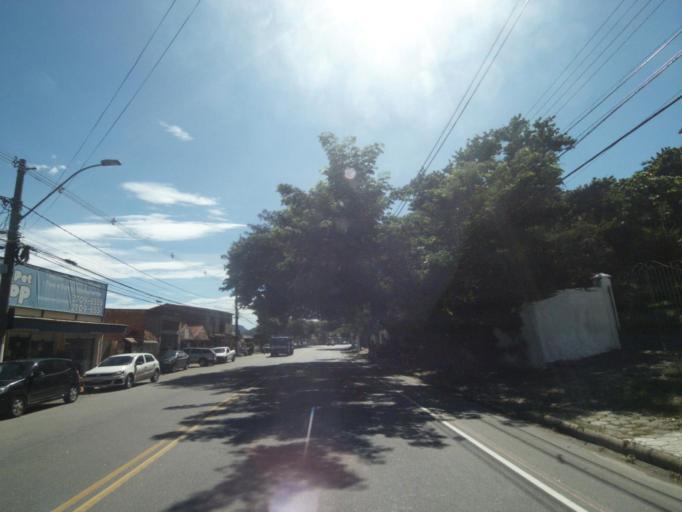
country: BR
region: Rio de Janeiro
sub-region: Niteroi
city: Niteroi
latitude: -22.9526
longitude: -43.0651
